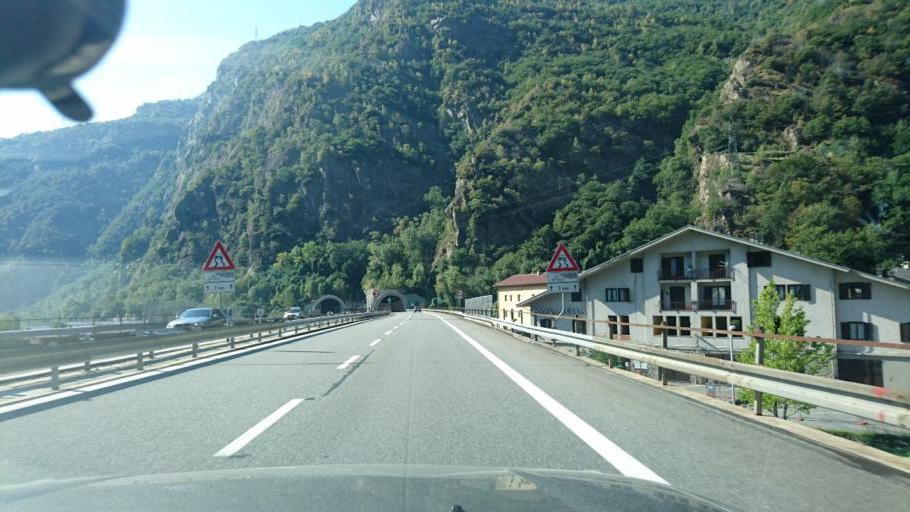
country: IT
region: Aosta Valley
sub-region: Valle d'Aosta
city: Hone
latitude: 45.6112
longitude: 7.7386
